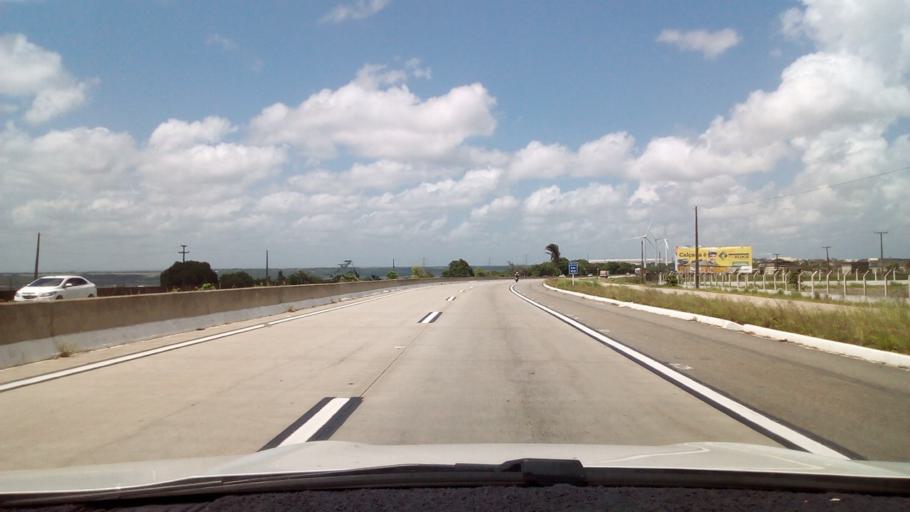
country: BR
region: Paraiba
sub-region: Conde
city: Conde
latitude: -7.2835
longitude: -34.9391
